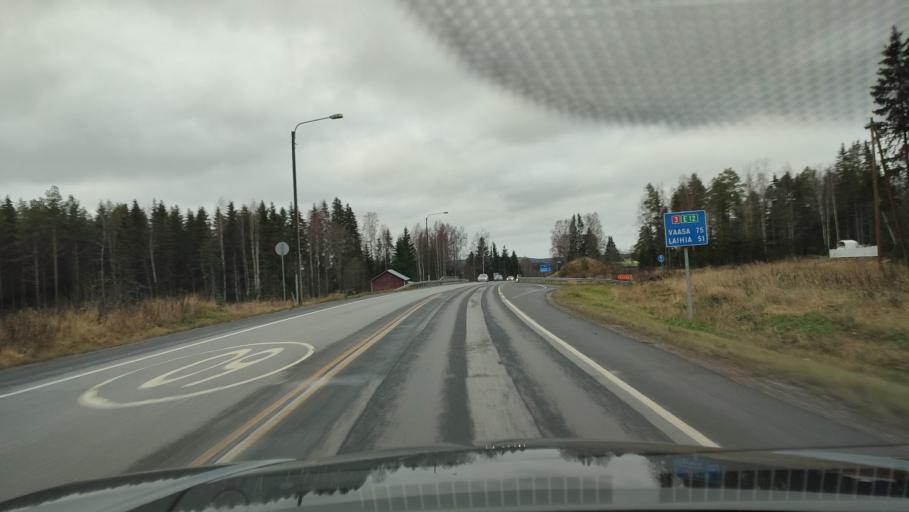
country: FI
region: Southern Ostrobothnia
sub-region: Seinaejoki
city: Kurikka
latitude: 62.6210
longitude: 22.4302
